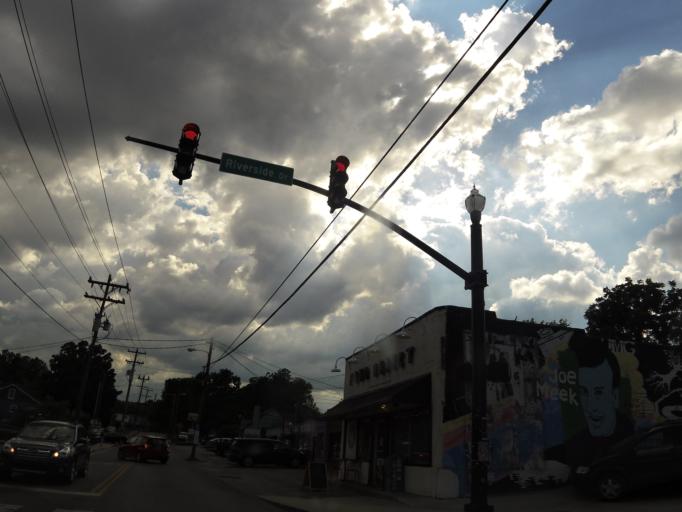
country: US
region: Tennessee
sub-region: Davidson County
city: Nashville
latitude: 36.2048
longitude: -86.7244
